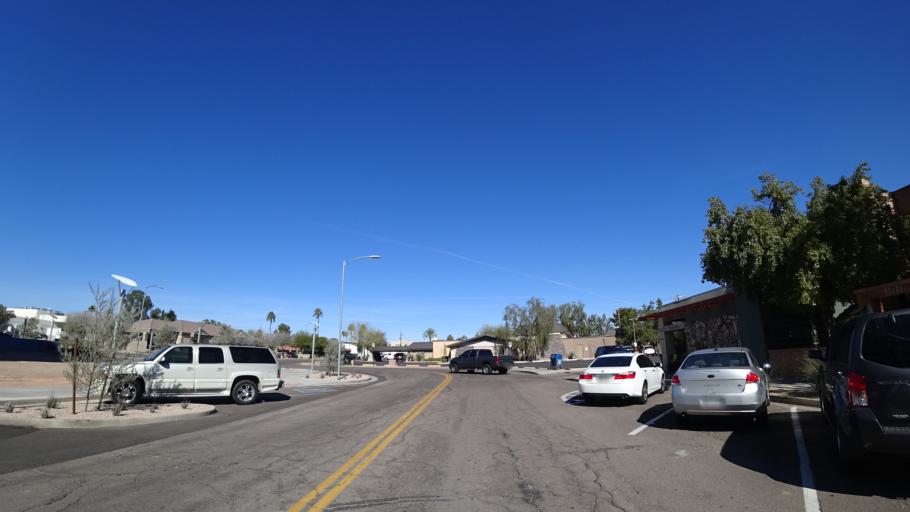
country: US
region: Arizona
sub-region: Maricopa County
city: Scottsdale
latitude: 33.5012
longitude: -111.9201
